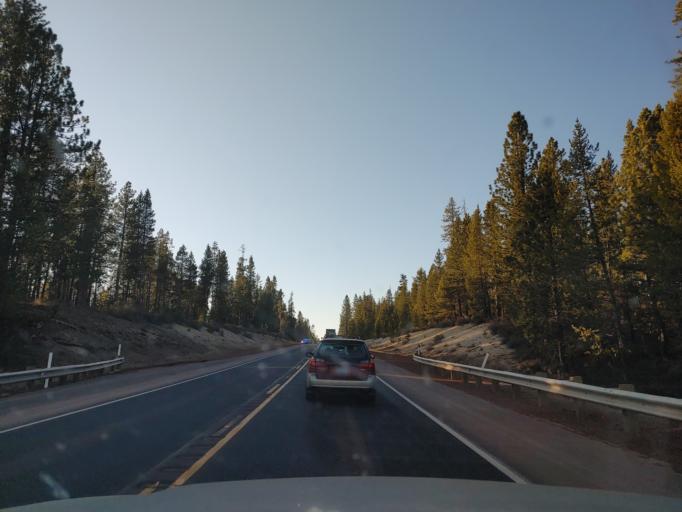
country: US
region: Oregon
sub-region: Deschutes County
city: La Pine
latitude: 43.3806
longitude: -121.8013
